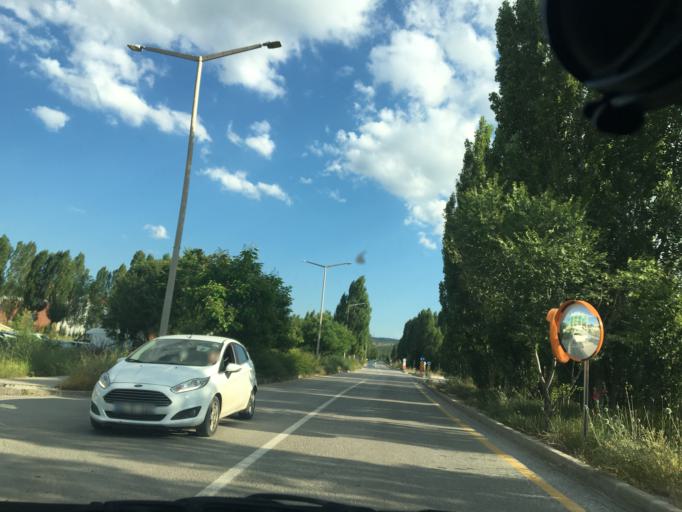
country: TR
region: Ankara
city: Ankara
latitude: 39.8948
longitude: 32.7771
